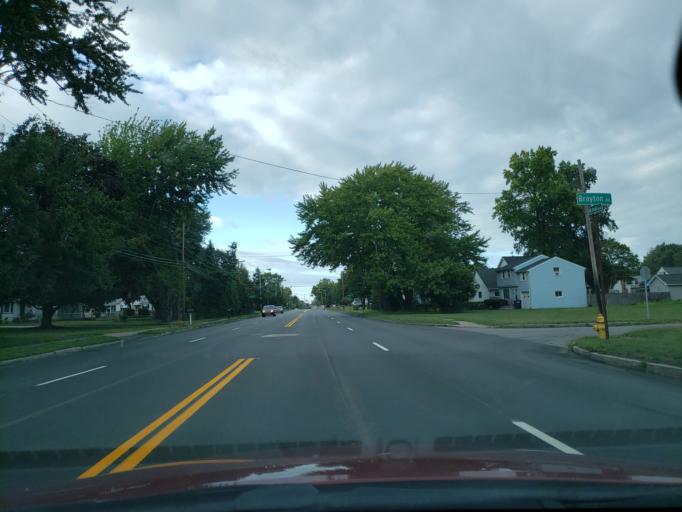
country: US
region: New York
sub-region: Monroe County
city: Greece
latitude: 43.2349
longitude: -77.6591
